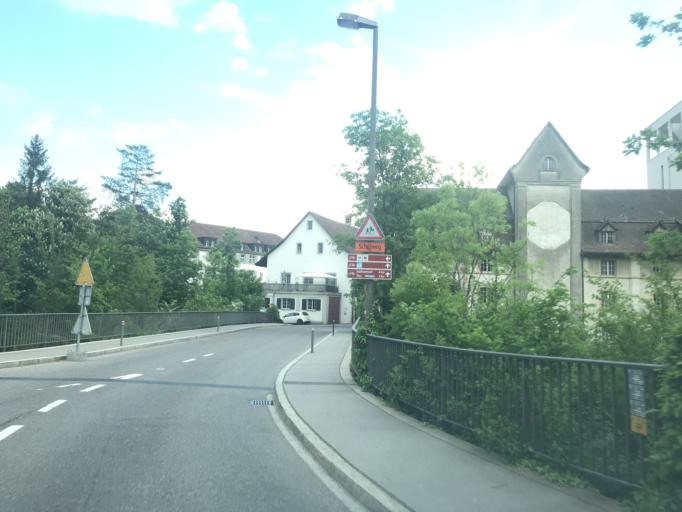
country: CH
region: Zurich
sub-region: Bezirk Winterthur
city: Wuelflingen (Kreis 6)
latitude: 47.5055
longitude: 8.6831
